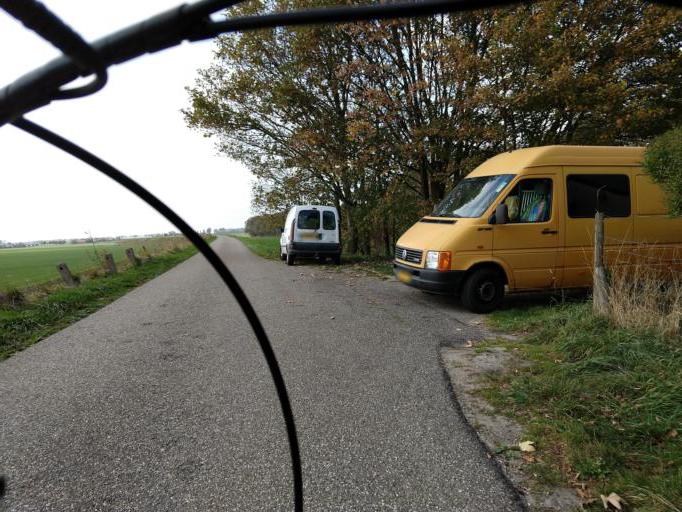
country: NL
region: Zeeland
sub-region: Schouwen-Duiveland
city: Bruinisse
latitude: 51.6758
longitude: 4.0012
